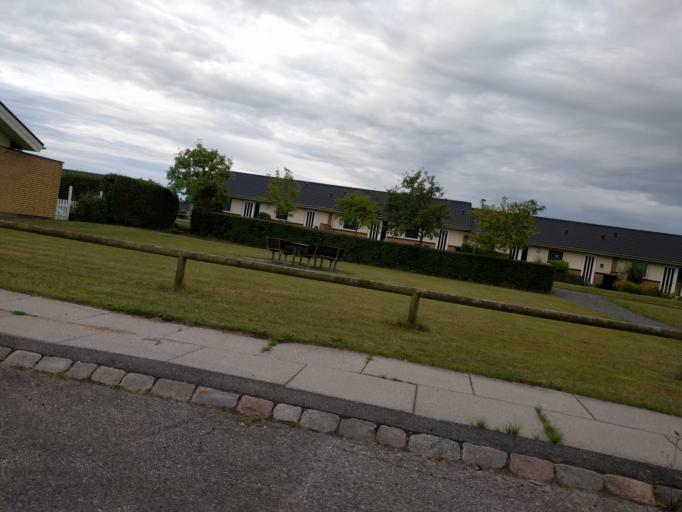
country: DK
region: South Denmark
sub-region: Kerteminde Kommune
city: Munkebo
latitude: 55.4667
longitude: 10.5630
